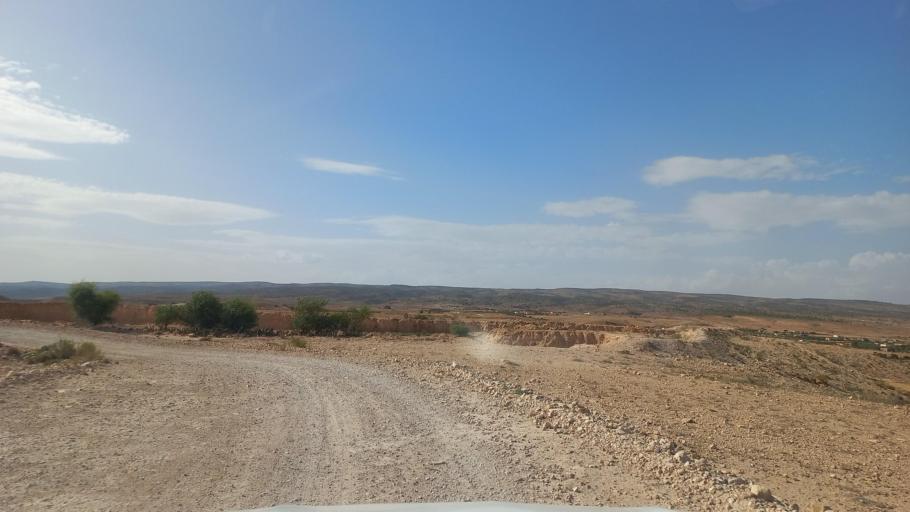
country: TN
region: Al Qasrayn
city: Kasserine
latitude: 35.2612
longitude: 8.9262
